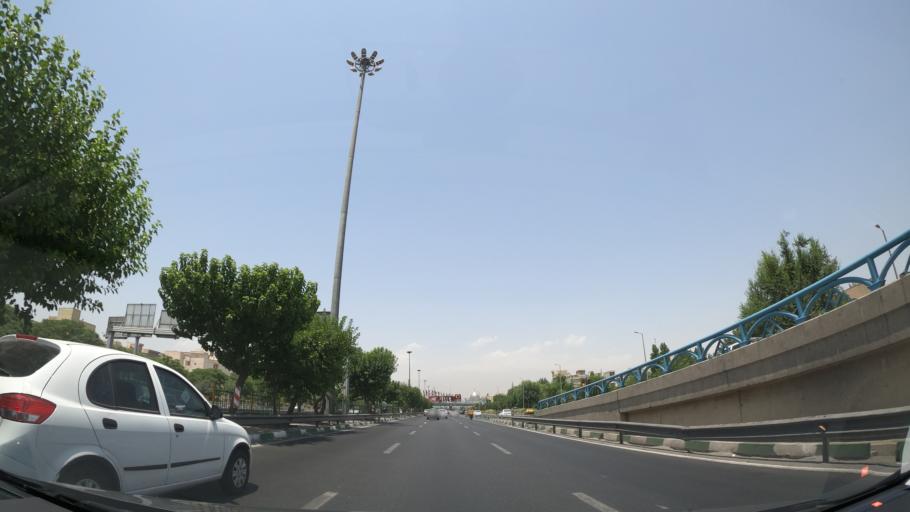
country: IR
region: Tehran
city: Tehran
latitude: 35.6657
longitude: 51.3819
